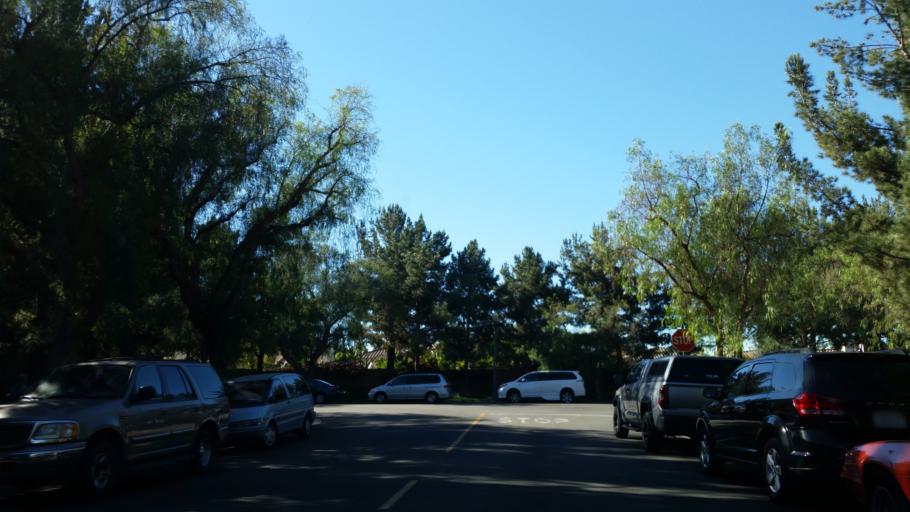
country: US
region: California
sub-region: Orange County
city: North Tustin
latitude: 33.7204
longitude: -117.7786
